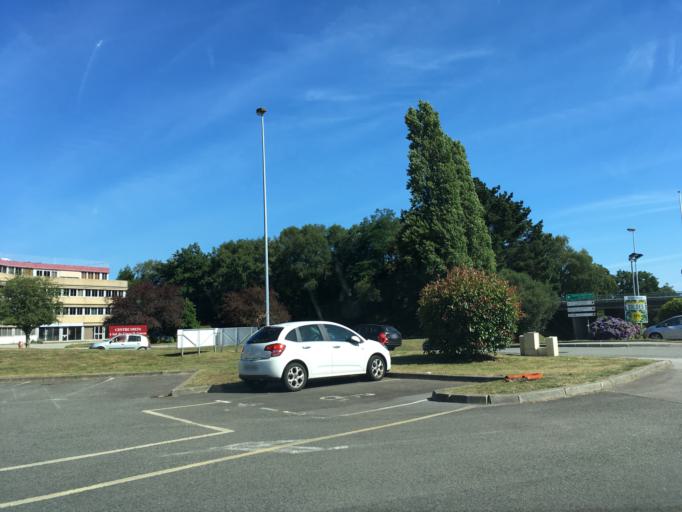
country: FR
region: Brittany
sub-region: Departement du Finistere
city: Quimper
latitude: 47.9811
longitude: -4.1038
